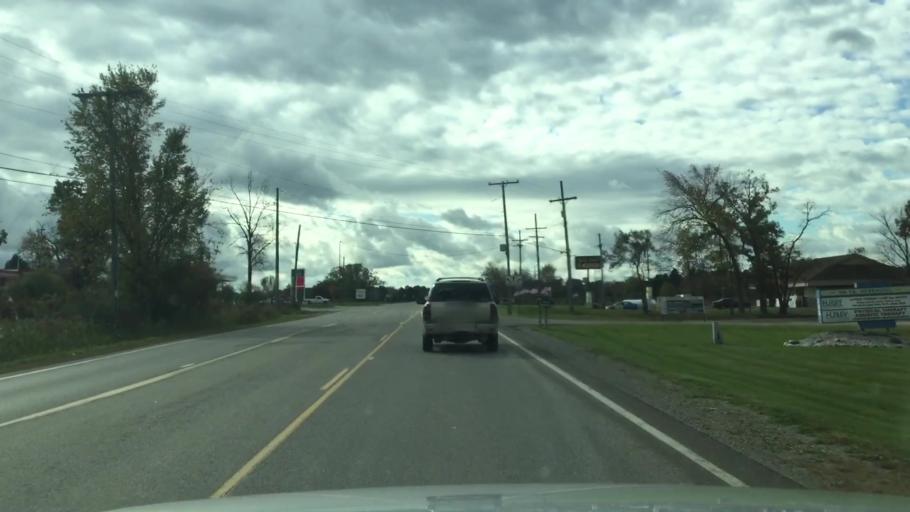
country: US
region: Michigan
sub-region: Lapeer County
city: Lapeer
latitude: 43.0362
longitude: -83.3617
